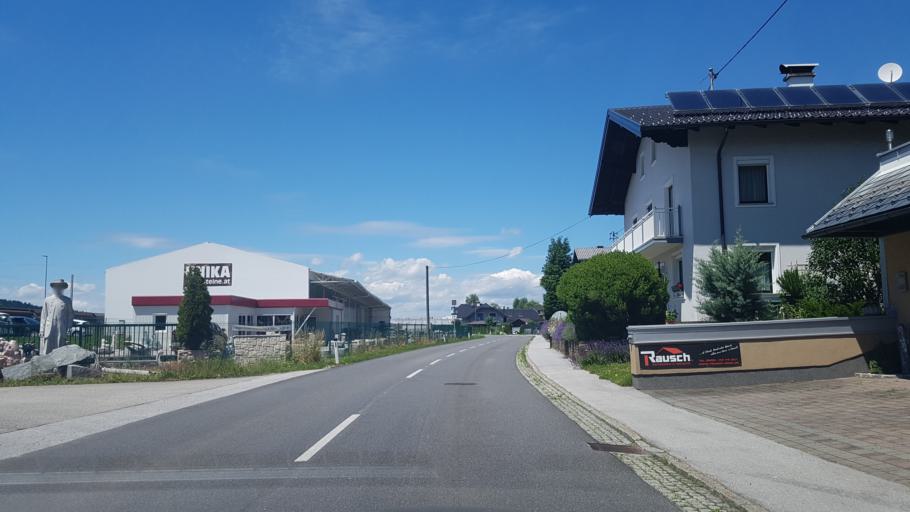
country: AT
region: Salzburg
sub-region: Politischer Bezirk Salzburg-Umgebung
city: Strasswalchen
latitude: 47.9972
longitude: 13.2349
